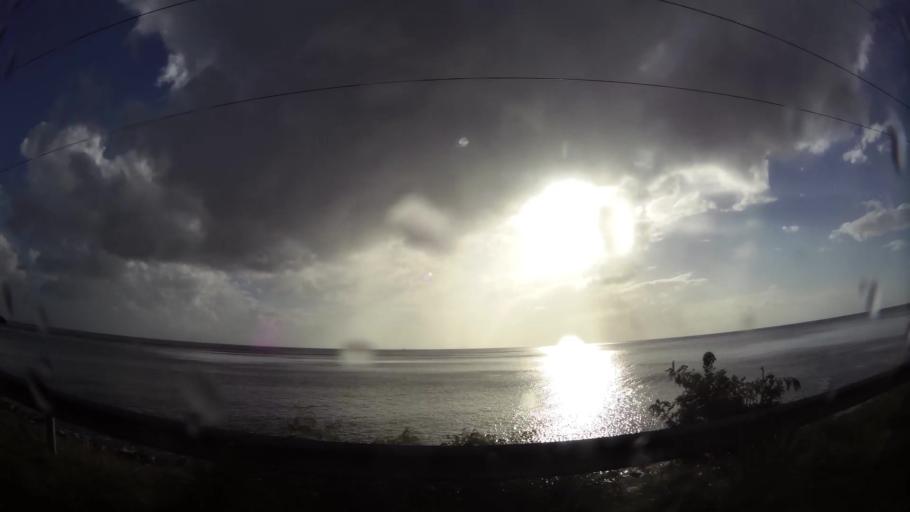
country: DM
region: Saint Joseph
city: Saint Joseph
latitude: 15.3865
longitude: -61.4140
